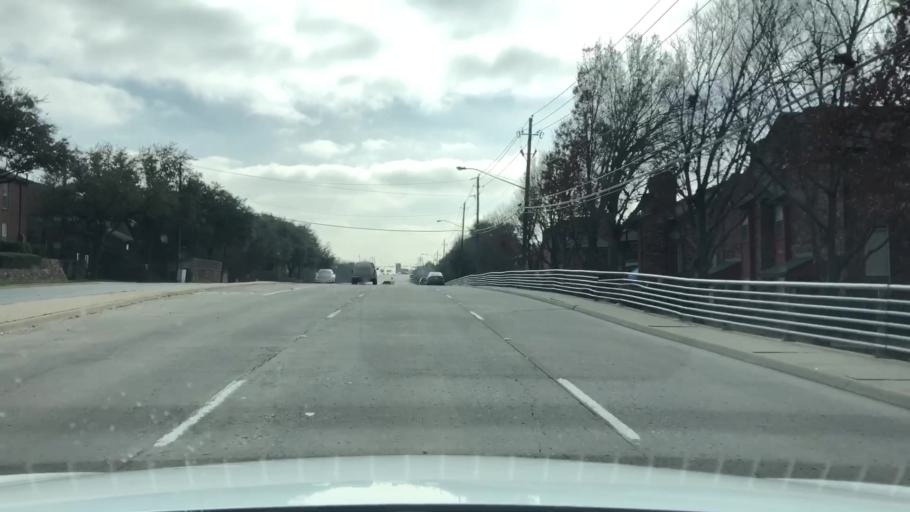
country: US
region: Texas
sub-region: Dallas County
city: Addison
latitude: 33.0084
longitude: -96.8574
